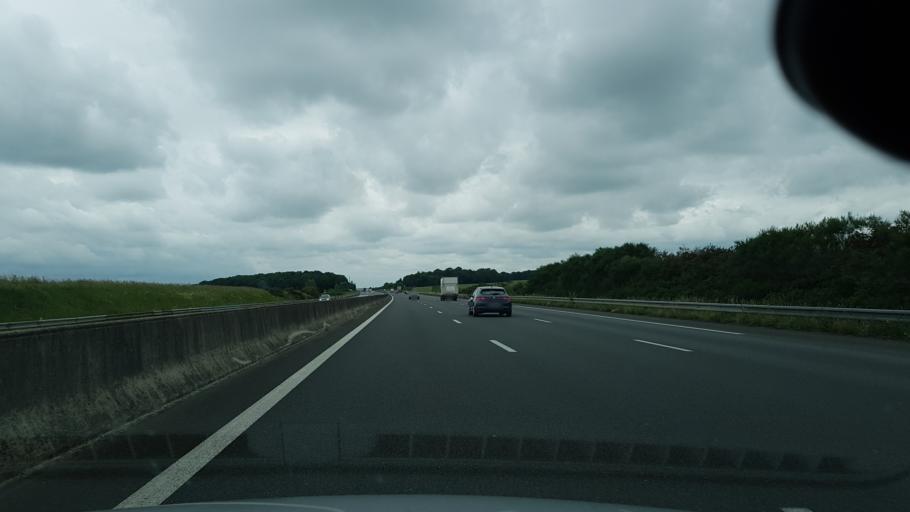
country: FR
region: Centre
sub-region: Departement du Loir-et-Cher
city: Herbault
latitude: 47.5801
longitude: 1.0660
